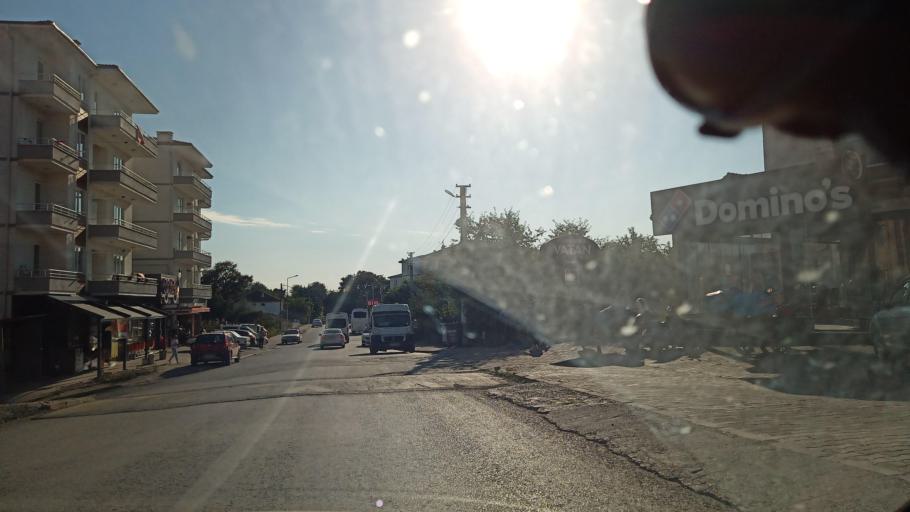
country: TR
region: Sakarya
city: Kazimpasa
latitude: 40.8579
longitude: 30.2878
